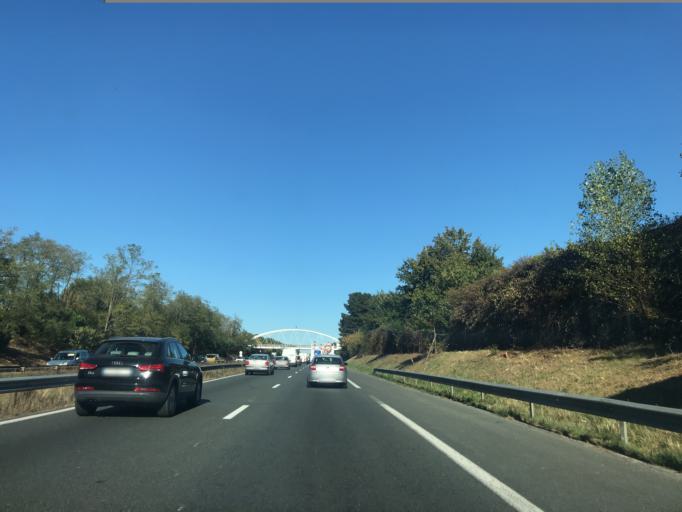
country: FR
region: Aquitaine
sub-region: Departement de la Gironde
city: Eysines
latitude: 44.8751
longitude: -0.6354
